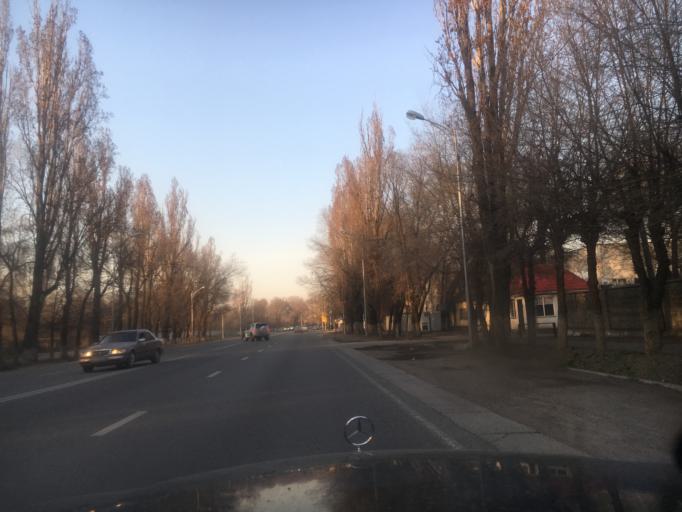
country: KZ
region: Almaty Oblysy
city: Pervomayskiy
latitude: 43.3497
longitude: 76.9711
